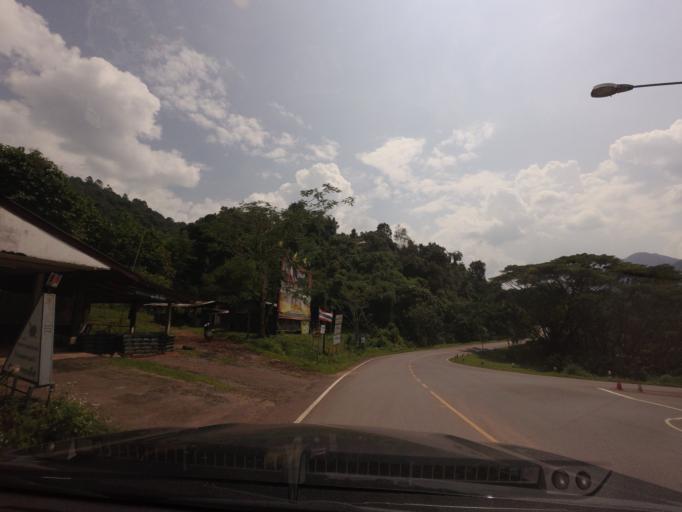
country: TH
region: Nan
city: Bo Kluea
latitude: 19.1520
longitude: 101.1576
